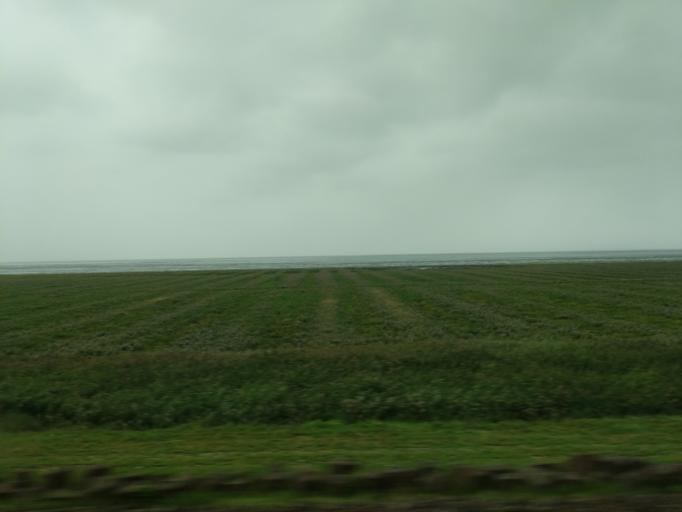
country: DE
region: Schleswig-Holstein
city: Friedrich-Wilhelm-Lubke-Koog
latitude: 54.8857
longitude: 8.5751
